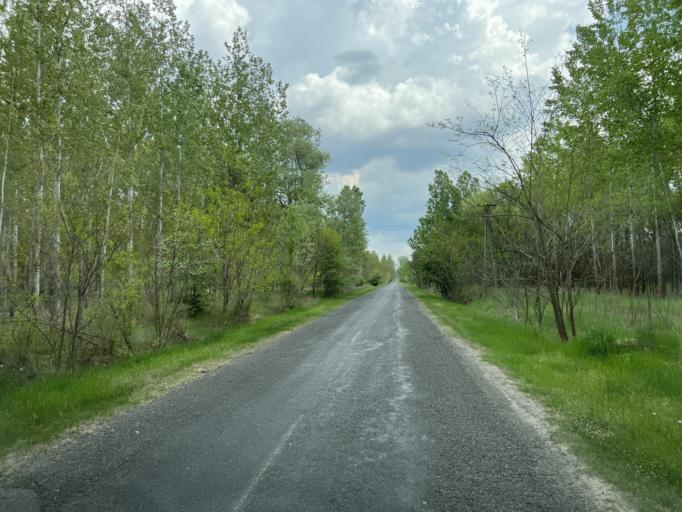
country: HU
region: Pest
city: Csemo
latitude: 47.0990
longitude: 19.7387
